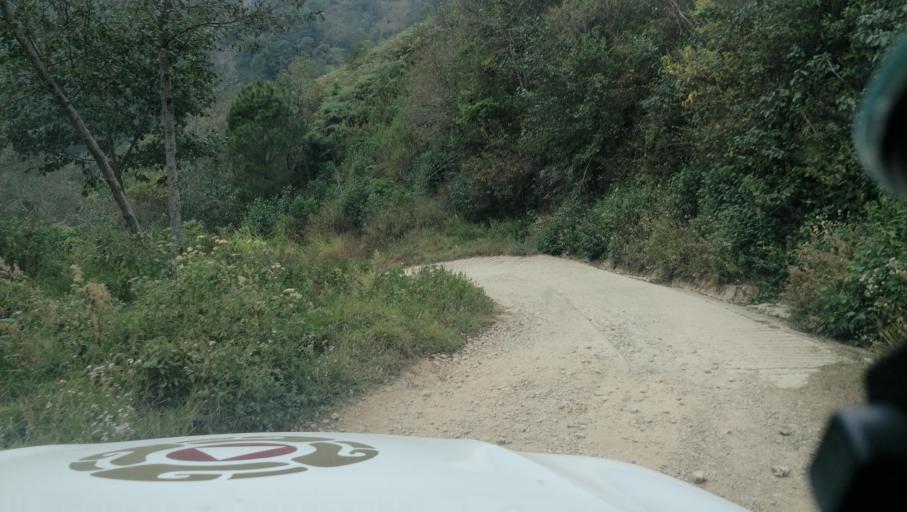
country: GT
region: San Marcos
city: Tacana
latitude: 15.2180
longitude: -92.2015
